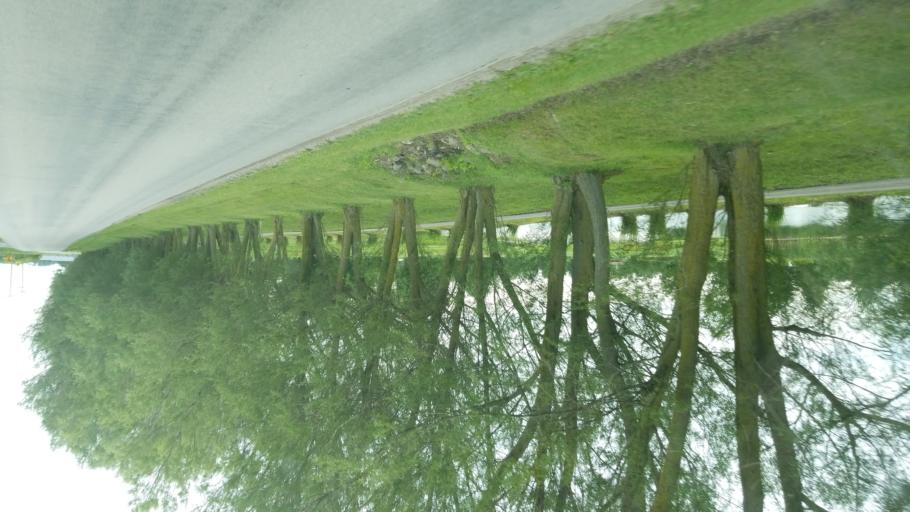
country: US
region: Ohio
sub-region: Knox County
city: Centerburg
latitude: 40.2903
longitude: -82.7050
